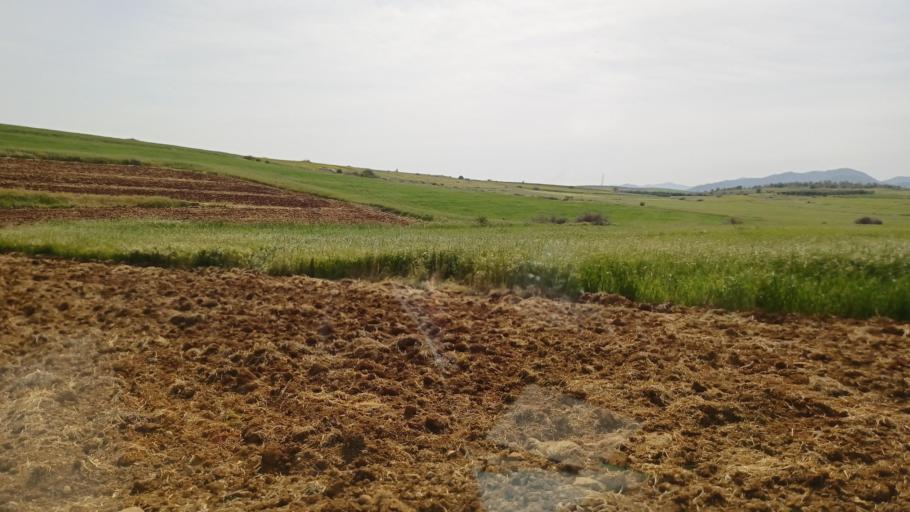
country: CY
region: Lefkosia
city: Astromeritis
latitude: 35.1030
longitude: 32.9608
